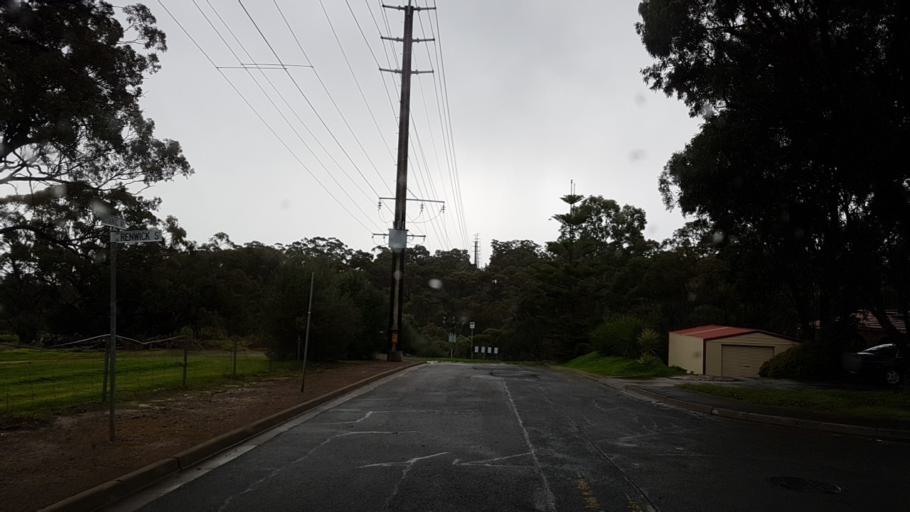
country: AU
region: South Australia
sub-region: Onkaparinga
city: Bedford Park
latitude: -35.0476
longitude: 138.5790
